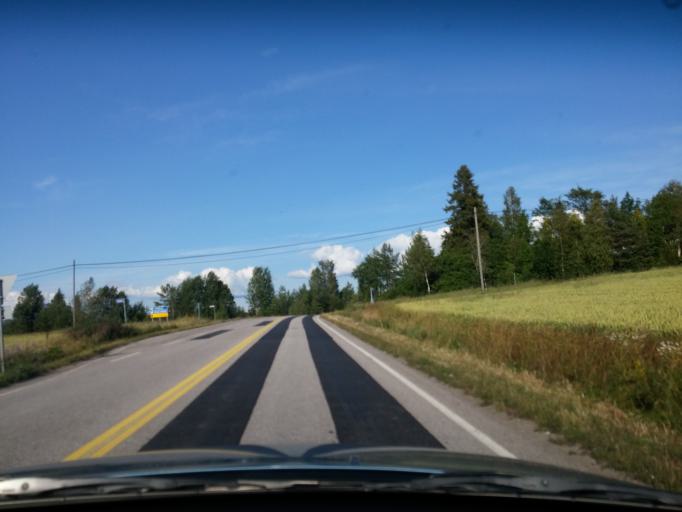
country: FI
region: Uusimaa
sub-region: Porvoo
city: Askola
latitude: 60.5157
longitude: 25.5153
